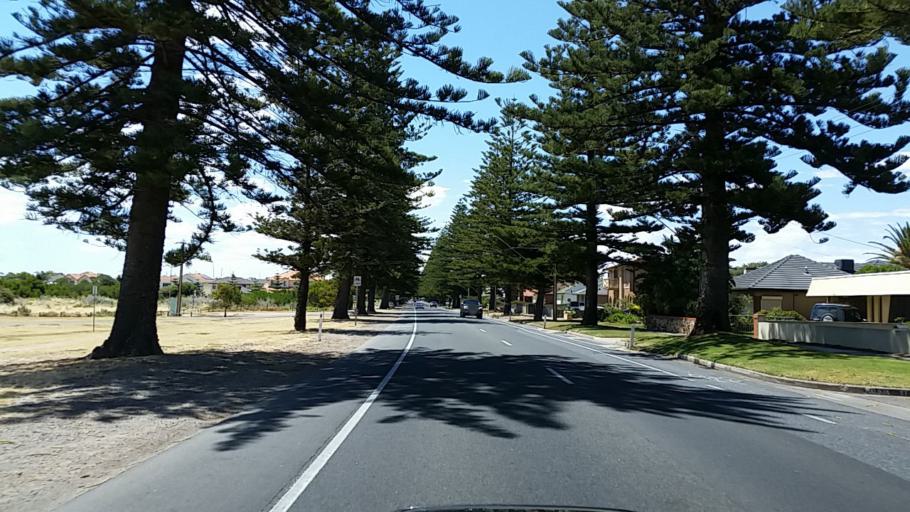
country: AU
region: South Australia
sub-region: Port Adelaide Enfield
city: Birkenhead
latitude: -34.7986
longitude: 138.4919
